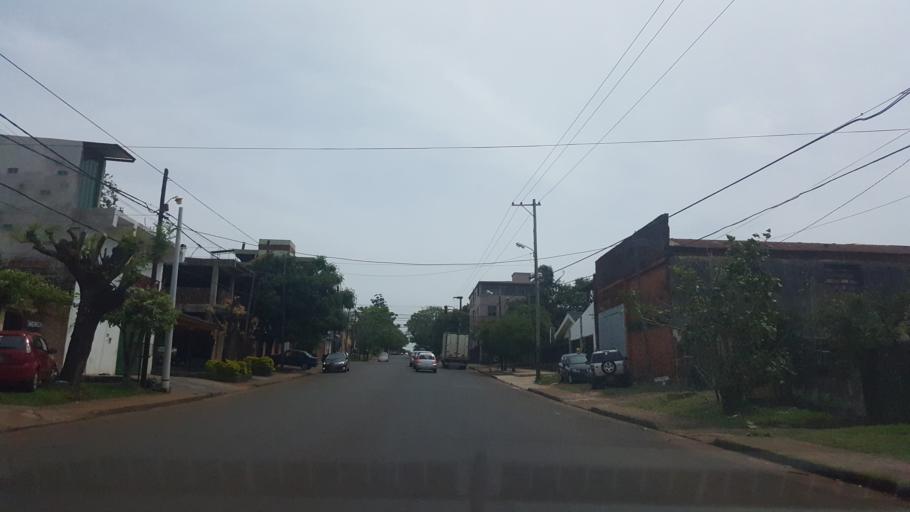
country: AR
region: Misiones
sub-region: Departamento de Capital
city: Posadas
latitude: -27.3902
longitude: -55.9074
